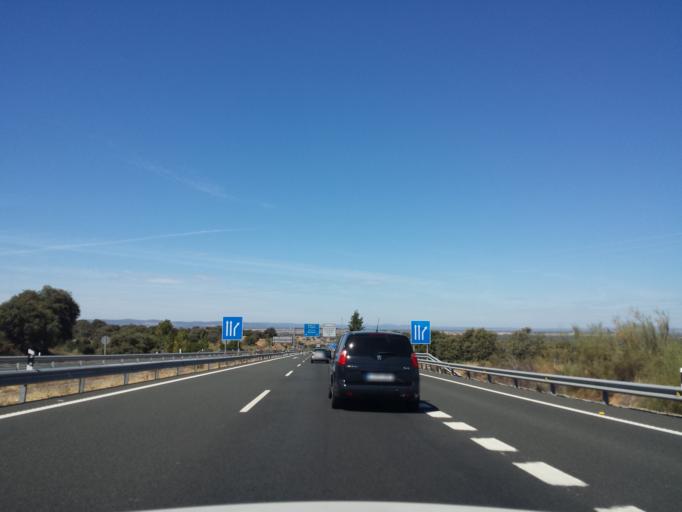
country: ES
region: Extremadura
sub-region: Provincia de Caceres
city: Millanes
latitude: 39.8725
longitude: -5.5684
